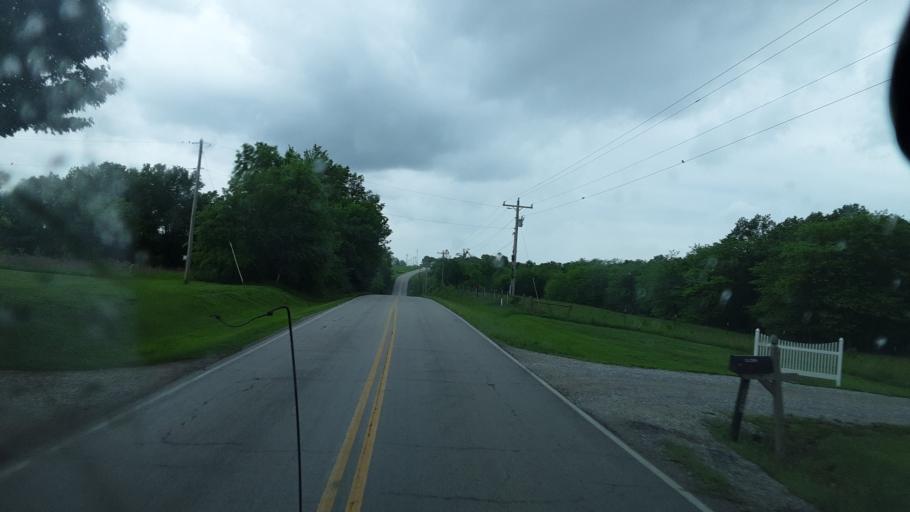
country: US
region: Missouri
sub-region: Monroe County
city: Paris
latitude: 39.4209
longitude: -92.2094
